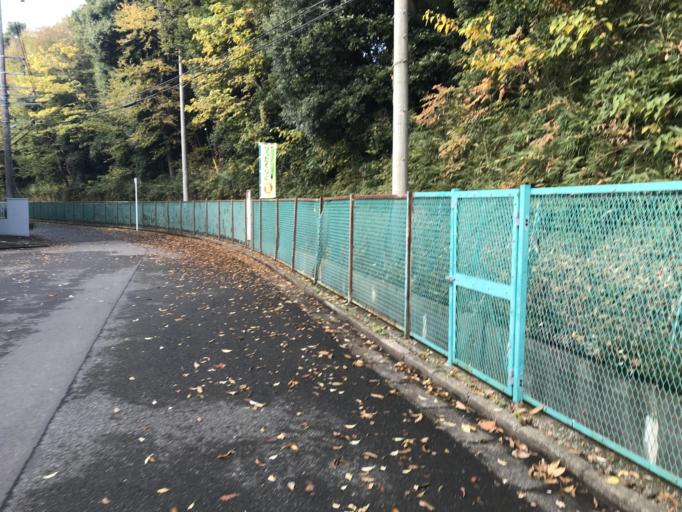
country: JP
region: Chiba
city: Funabashi
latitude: 35.7250
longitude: 139.9704
